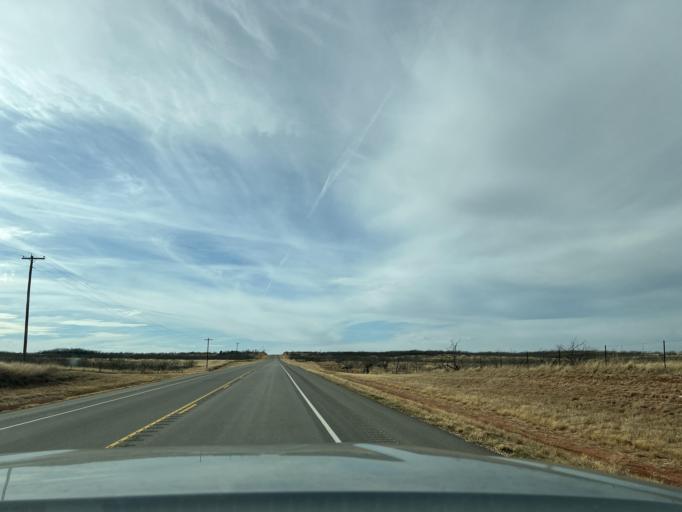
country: US
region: Texas
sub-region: Jones County
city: Anson
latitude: 32.7508
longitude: -99.7374
